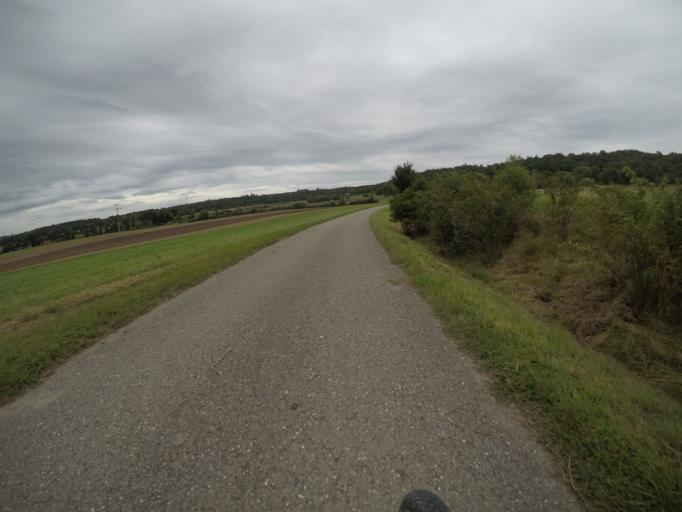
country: DE
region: Baden-Wuerttemberg
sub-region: Regierungsbezirk Stuttgart
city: Ehningen
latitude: 48.6319
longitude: 8.9391
